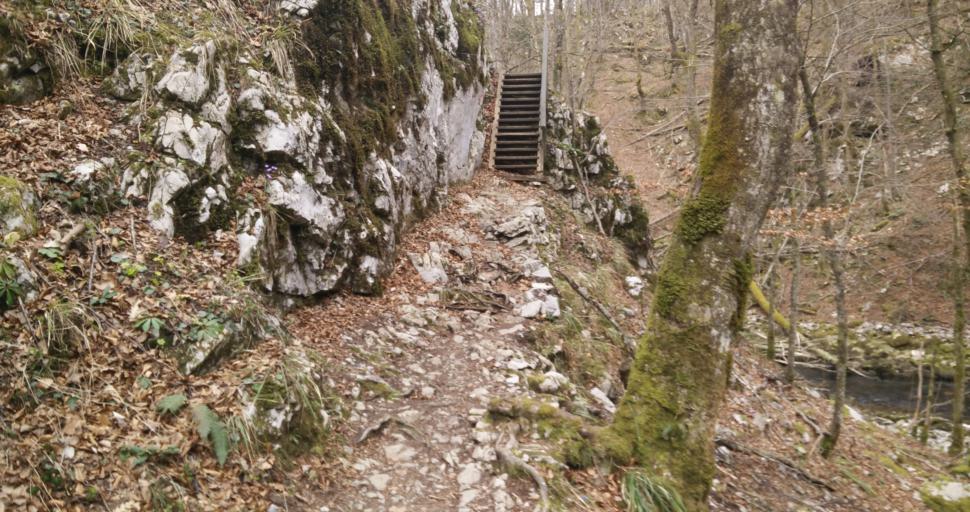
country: HR
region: Primorsko-Goranska
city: Vrbovsko
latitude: 45.3628
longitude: 15.0676
